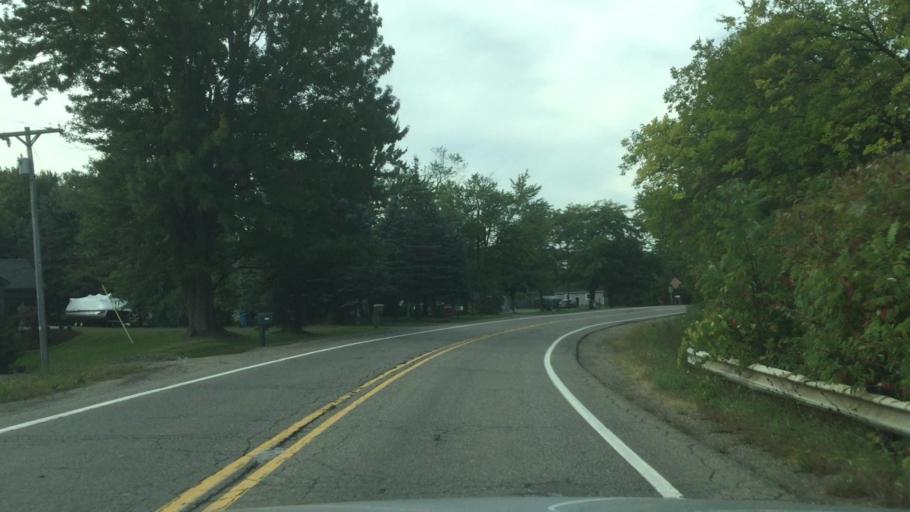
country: US
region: Michigan
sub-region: Oakland County
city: Holly
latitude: 42.8094
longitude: -83.6168
